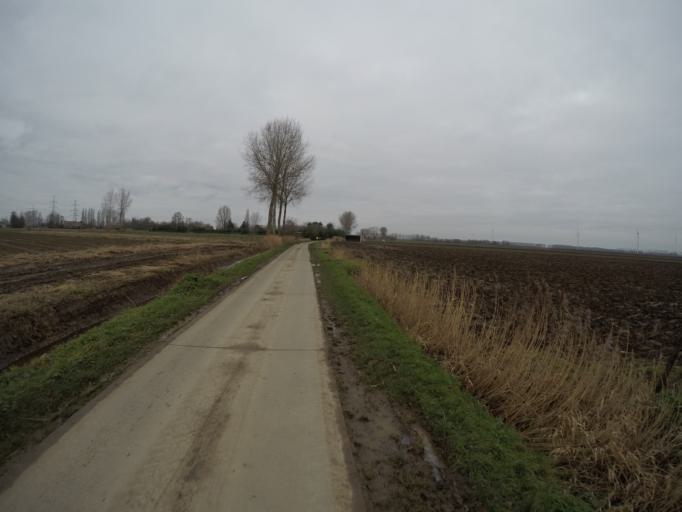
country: BE
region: Flanders
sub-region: Provincie Oost-Vlaanderen
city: Beveren
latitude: 51.2314
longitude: 4.2403
